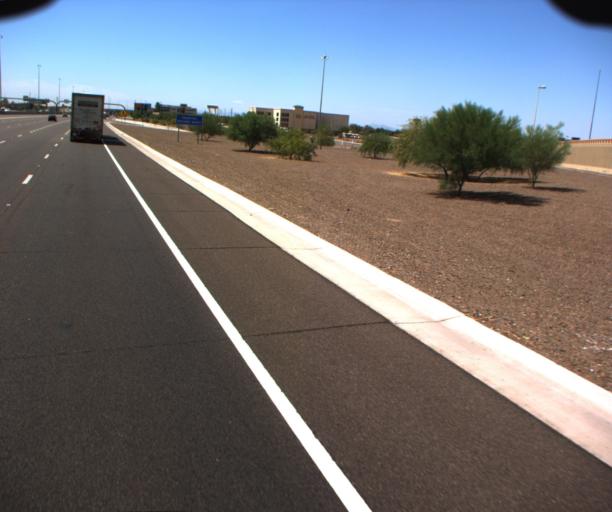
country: US
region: Arizona
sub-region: Maricopa County
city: Peoria
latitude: 33.6860
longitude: -112.1127
